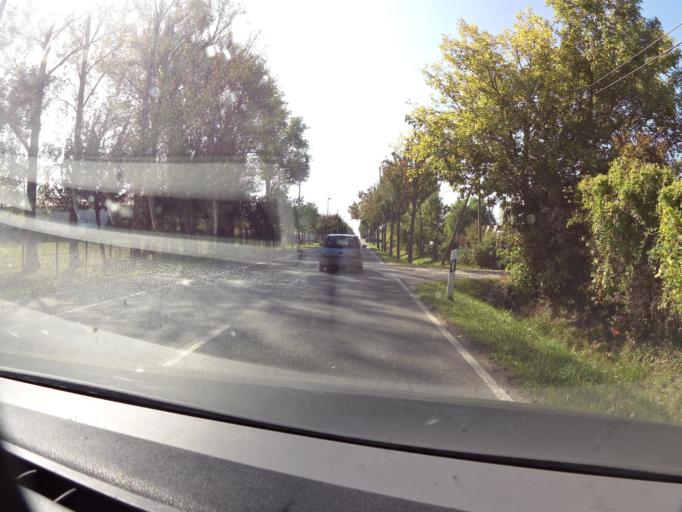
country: DE
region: Saxony-Anhalt
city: Diesdorf
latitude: 52.0854
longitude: 11.5657
